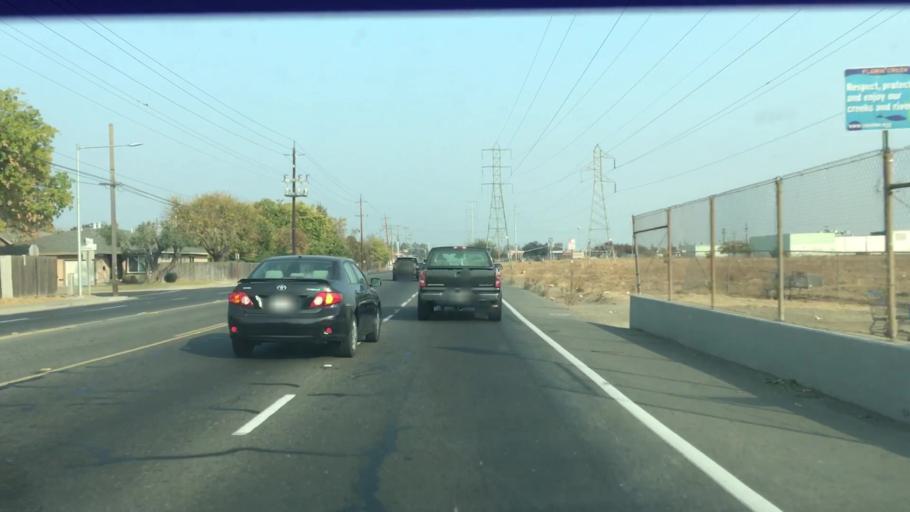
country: US
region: California
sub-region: Sacramento County
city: Florin
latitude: 38.4924
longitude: -121.4089
